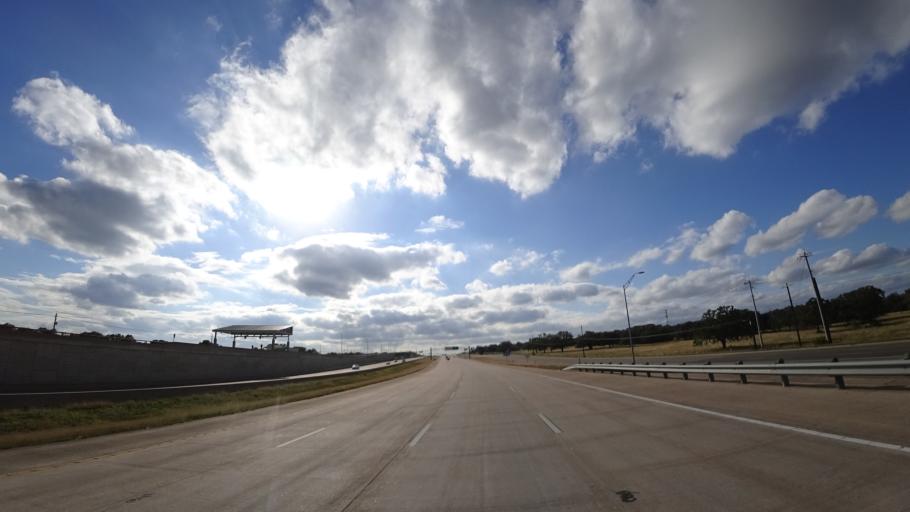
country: US
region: Texas
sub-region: Williamson County
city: Brushy Creek
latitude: 30.4813
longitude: -97.7506
